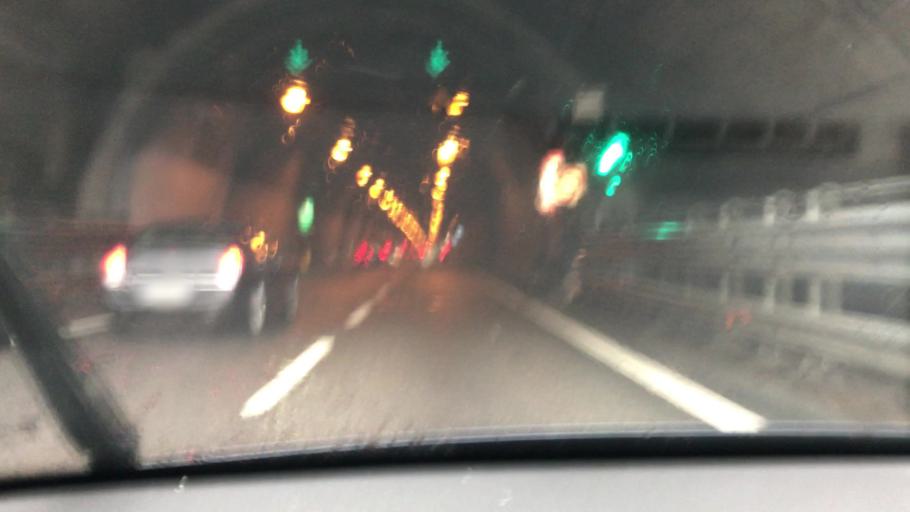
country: IT
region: Lombardy
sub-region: Provincia di Lecco
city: Dervio
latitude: 46.0763
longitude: 9.3152
